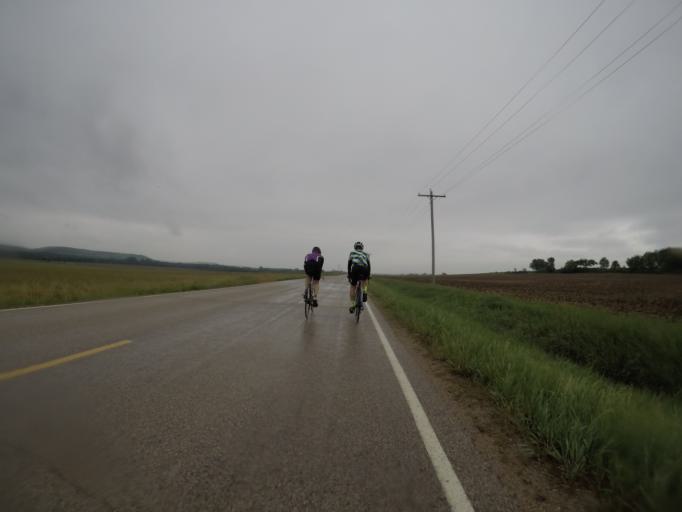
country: US
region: Kansas
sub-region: Pottawatomie County
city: Wamego
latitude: 39.3649
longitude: -96.2212
